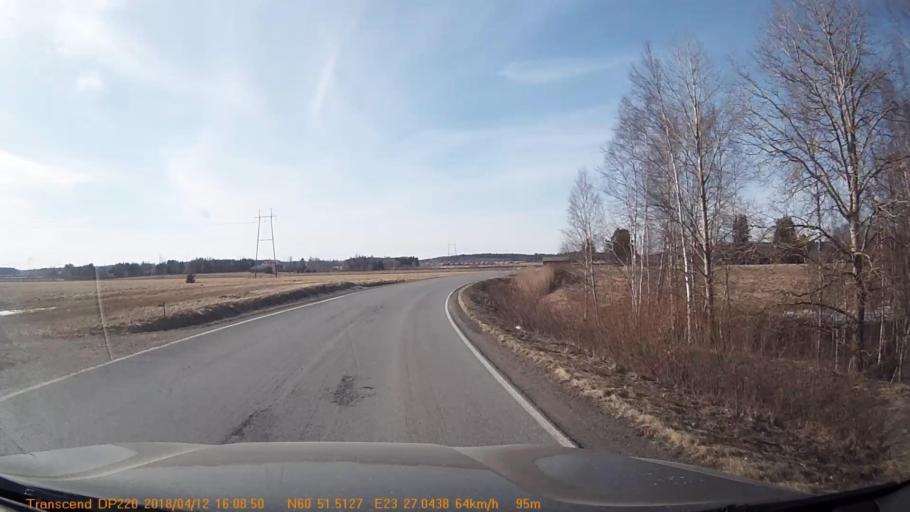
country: FI
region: Haeme
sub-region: Forssa
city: Jokioinen
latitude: 60.8582
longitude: 23.4511
